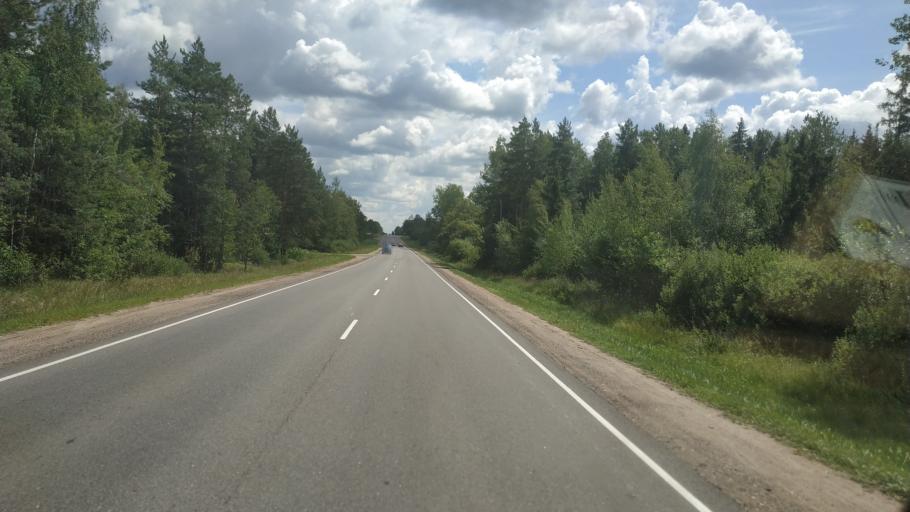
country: BY
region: Mogilev
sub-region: Mahilyowski Rayon
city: Veyno
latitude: 53.8234
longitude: 30.4271
